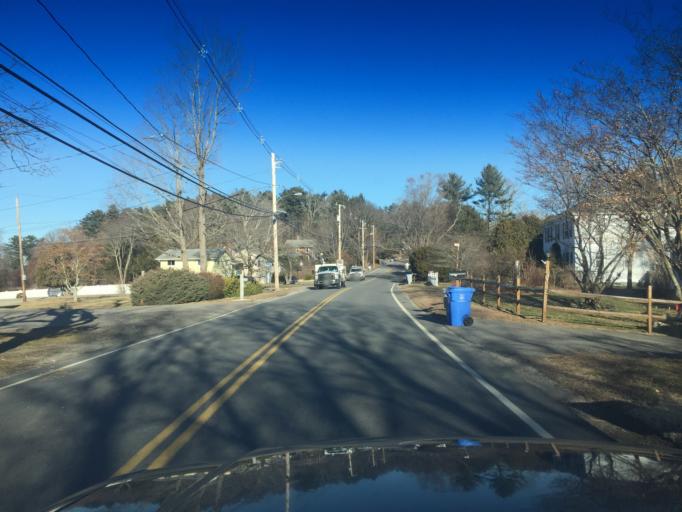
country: US
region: Massachusetts
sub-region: Middlesex County
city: Holliston
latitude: 42.1865
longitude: -71.4152
